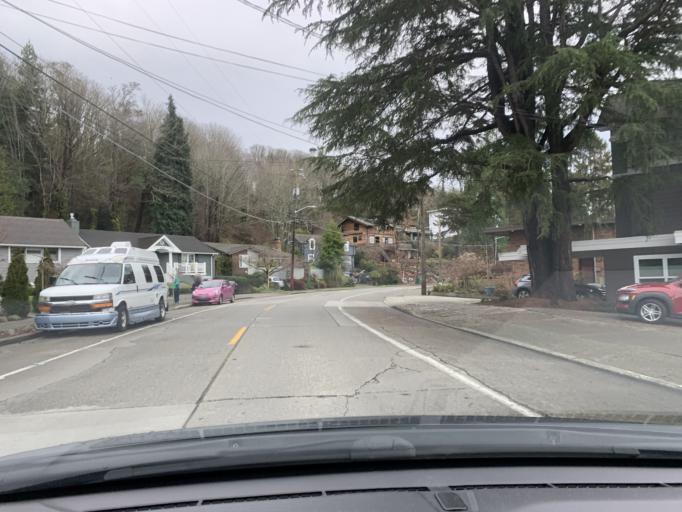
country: US
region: Washington
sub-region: King County
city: White Center
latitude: 47.5533
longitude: -122.3986
